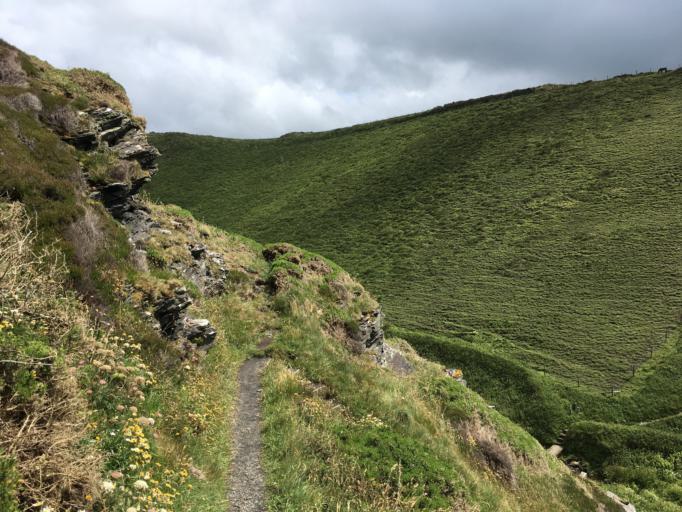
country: GB
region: England
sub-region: Cornwall
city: Camelford
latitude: 50.6971
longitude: -4.6795
